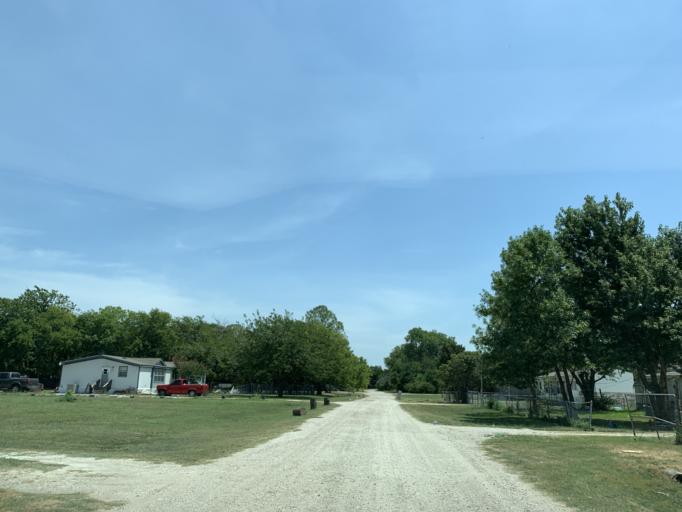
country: US
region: Texas
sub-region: Dallas County
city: Cedar Hill
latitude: 32.6423
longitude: -97.0253
